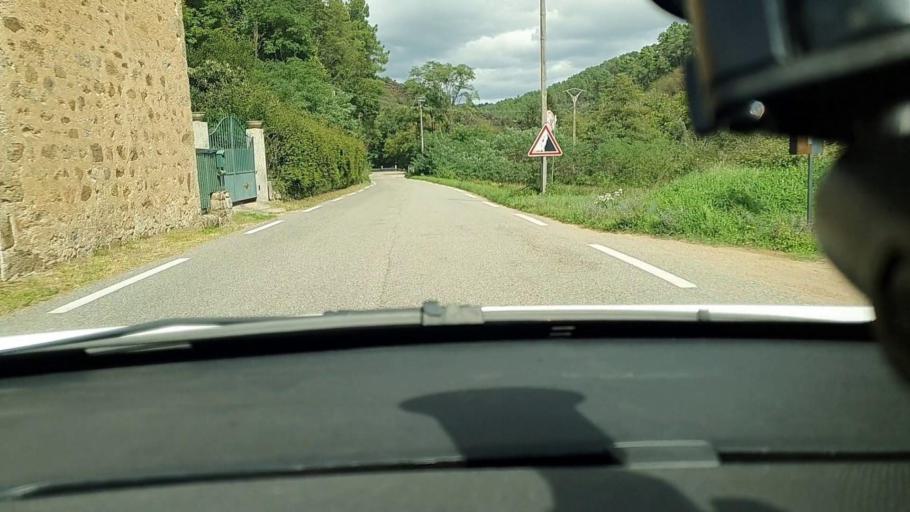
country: FR
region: Languedoc-Roussillon
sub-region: Departement du Gard
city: Laval-Pradel
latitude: 44.2481
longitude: 4.0596
